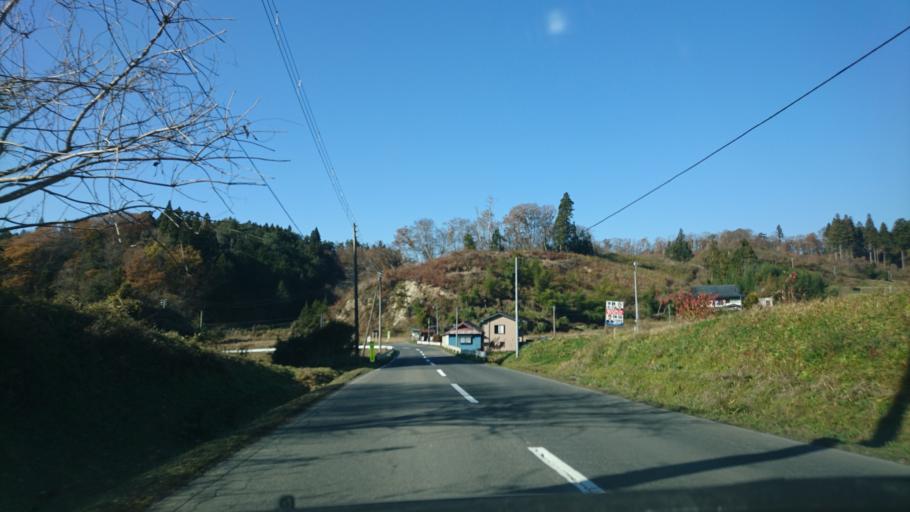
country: JP
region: Iwate
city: Ichinoseki
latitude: 38.9030
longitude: 141.4013
